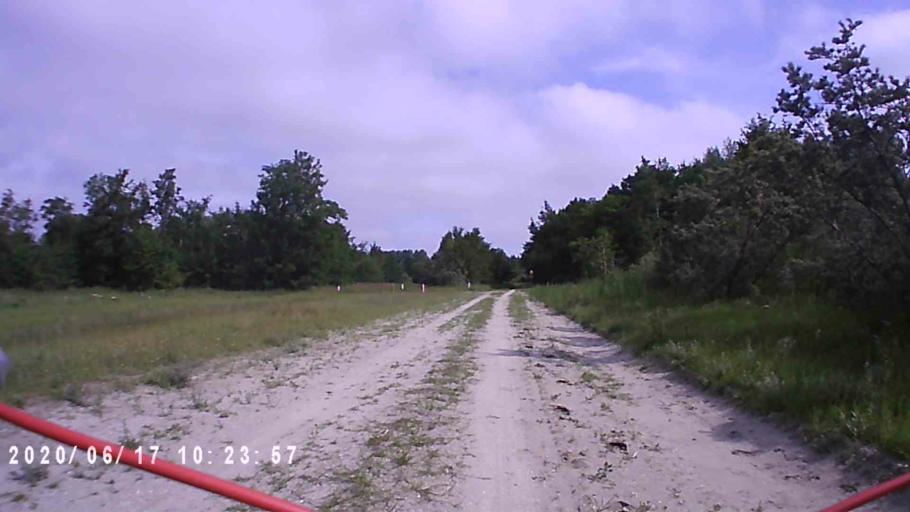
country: NL
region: Groningen
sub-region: Gemeente De Marne
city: Ulrum
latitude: 53.3909
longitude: 6.2477
